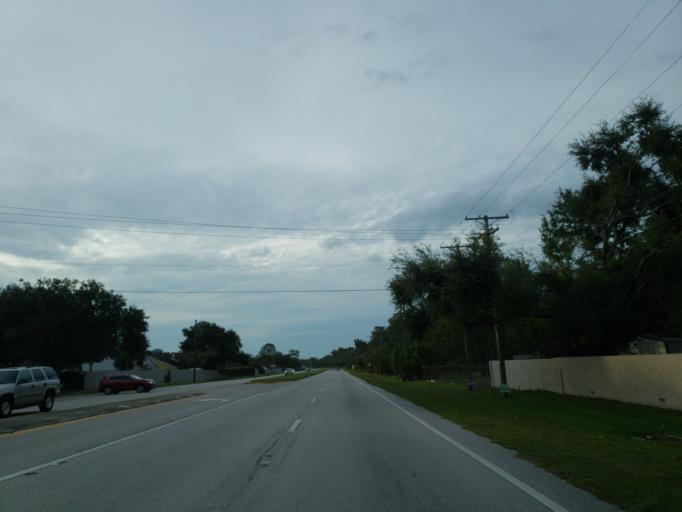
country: US
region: Florida
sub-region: Hillsborough County
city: Carrollwood Village
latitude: 28.0529
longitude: -82.5246
